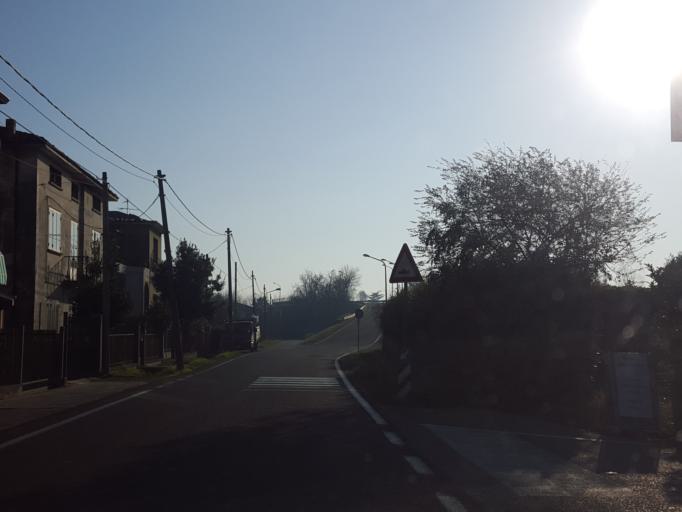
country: IT
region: Veneto
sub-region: Provincia di Vicenza
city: Lisiera
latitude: 45.5712
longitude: 11.5936
